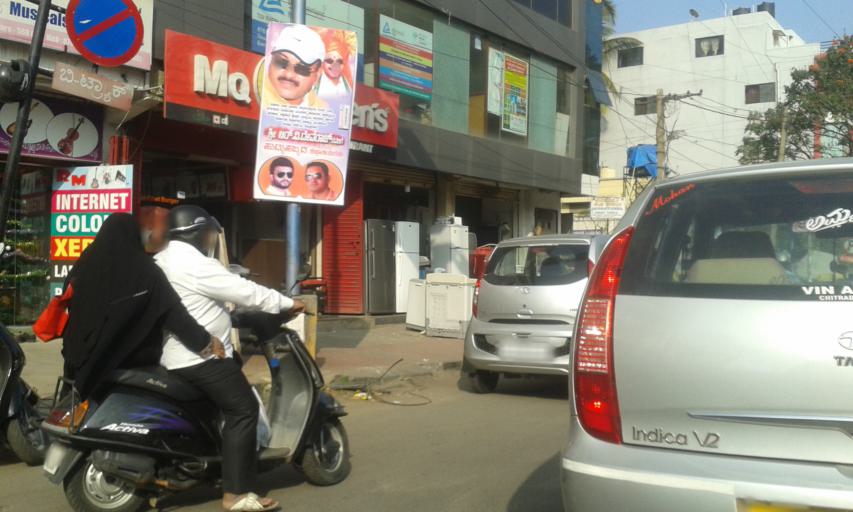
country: IN
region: Karnataka
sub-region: Bangalore Urban
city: Bangalore
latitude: 12.9284
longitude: 77.5972
